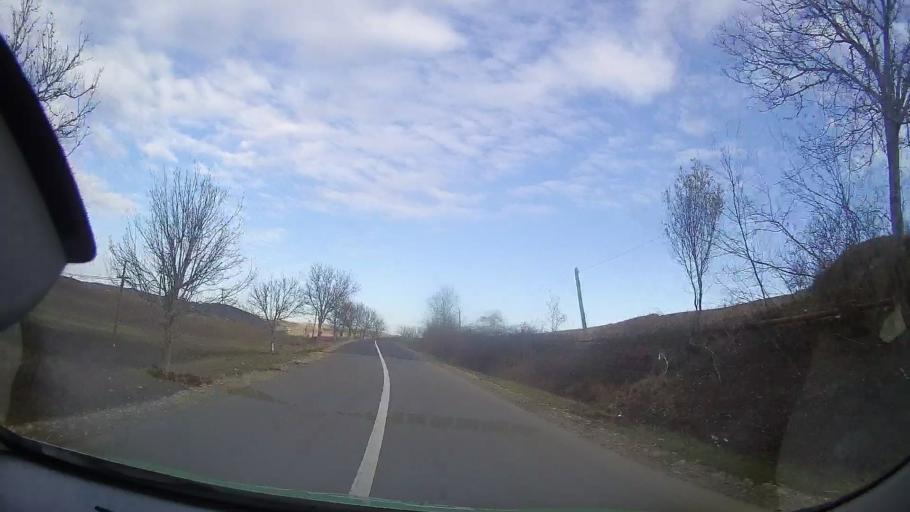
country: RO
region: Mures
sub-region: Comuna Iclanzel
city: Iclanzel
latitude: 46.5098
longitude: 24.2681
